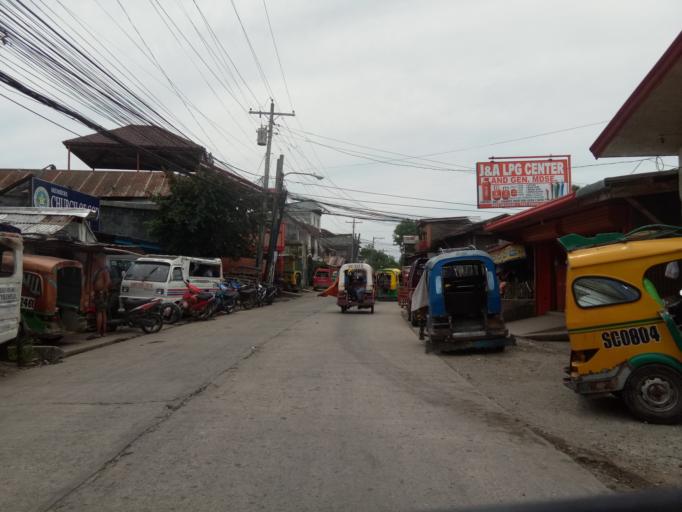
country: PH
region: Caraga
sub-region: Province of Surigao del Norte
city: Surigao
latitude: 9.7868
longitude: 125.4883
